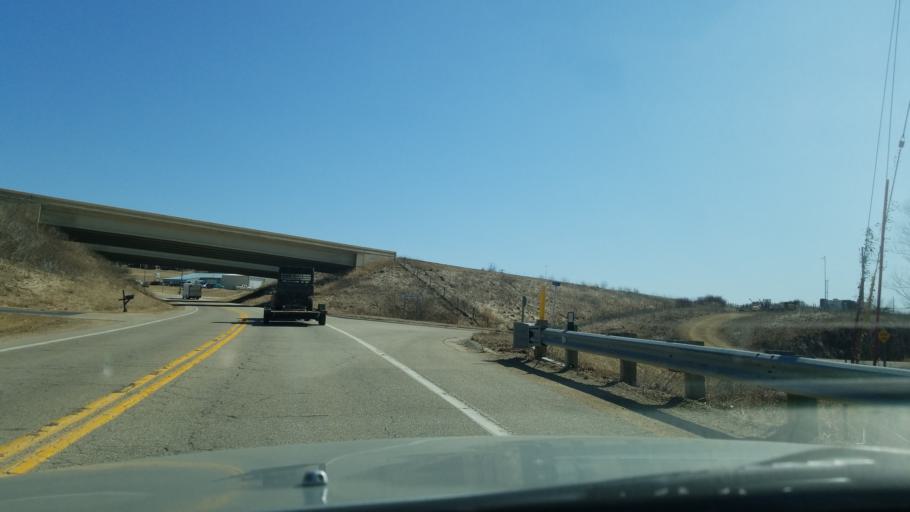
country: US
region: Wisconsin
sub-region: Iowa County
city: Mineral Point
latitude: 42.8622
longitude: -90.2037
